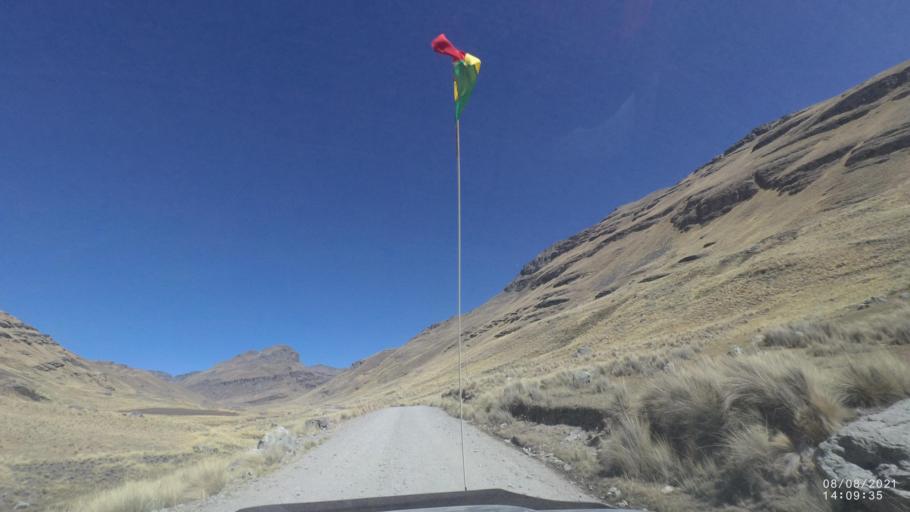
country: BO
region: Cochabamba
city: Sipe Sipe
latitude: -17.1462
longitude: -66.4371
